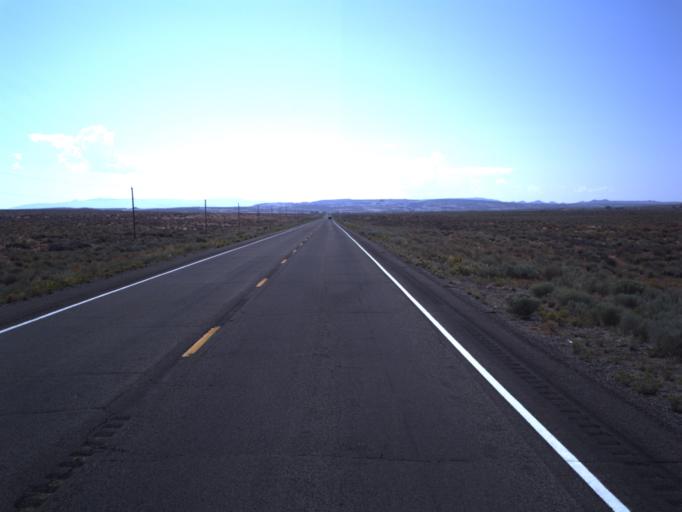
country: US
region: Utah
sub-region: San Juan County
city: Blanding
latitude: 37.1444
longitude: -109.5614
